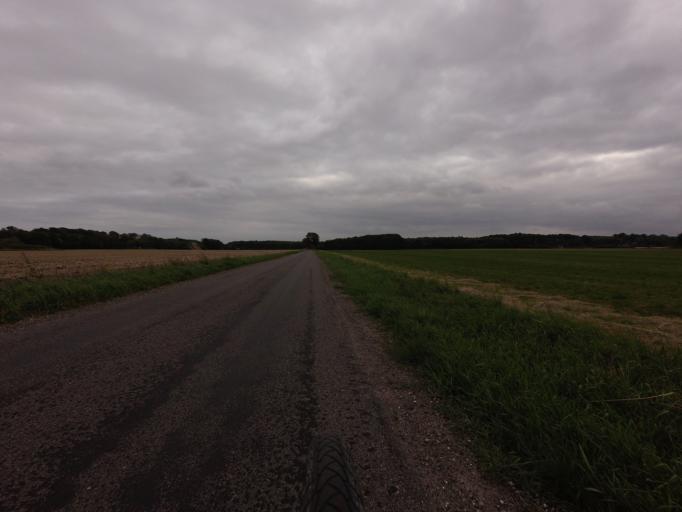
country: DK
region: Zealand
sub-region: Stevns Kommune
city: Store Heddinge
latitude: 55.3242
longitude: 12.3326
